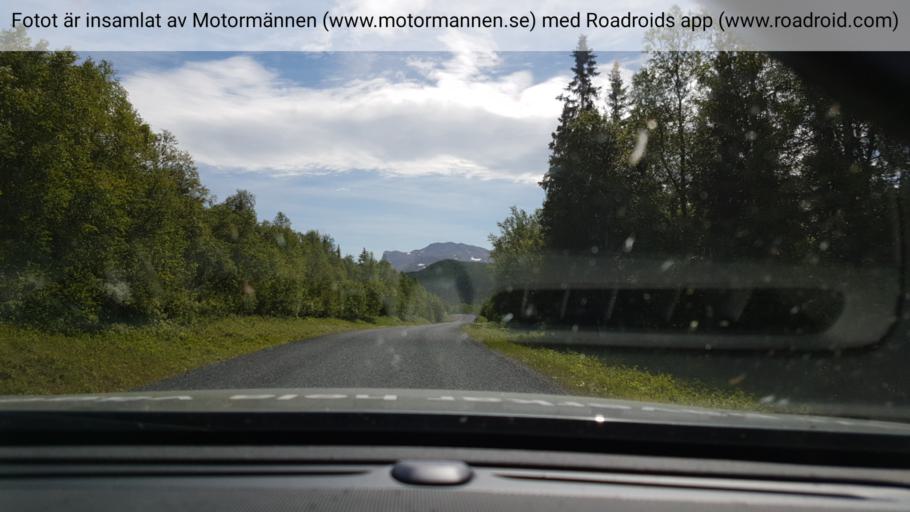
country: SE
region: Vaesterbotten
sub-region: Vilhelmina Kommun
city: Sjoberg
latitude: 65.2827
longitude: 15.2991
